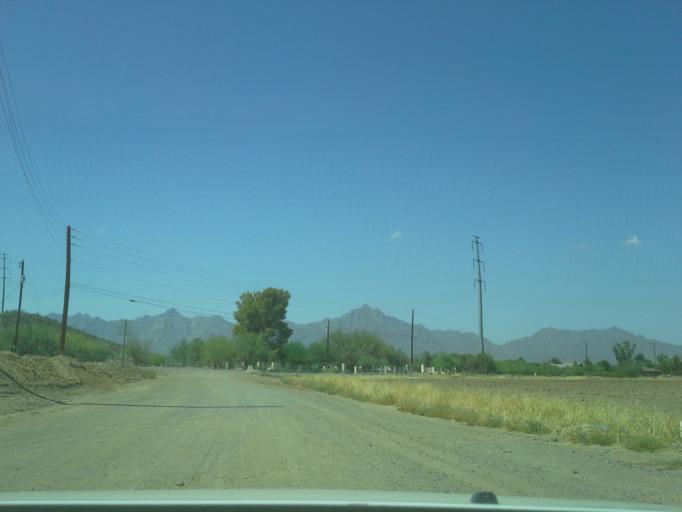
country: US
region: Arizona
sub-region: Maricopa County
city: Laveen
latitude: 33.3491
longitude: -112.1630
